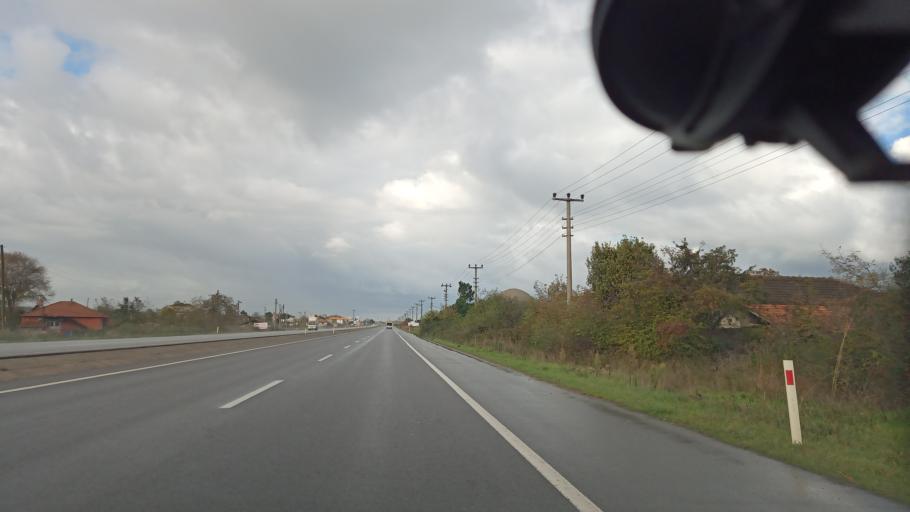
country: TR
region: Sakarya
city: Karasu
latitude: 41.0789
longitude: 30.7747
